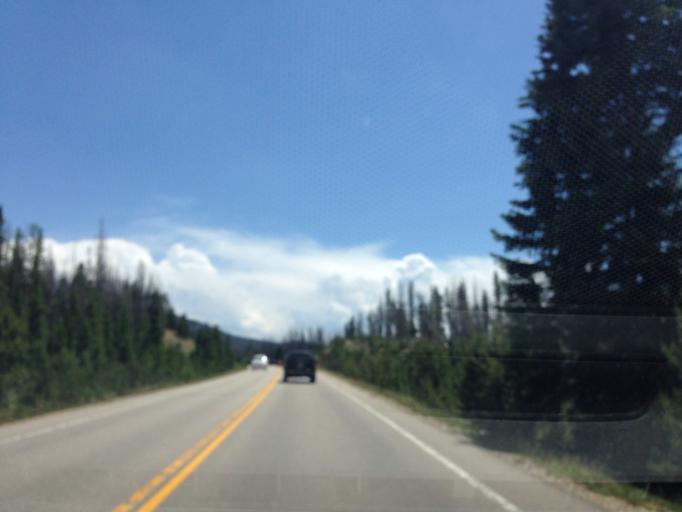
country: US
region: Colorado
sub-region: Grand County
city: Granby
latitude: 40.2694
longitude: -105.8344
